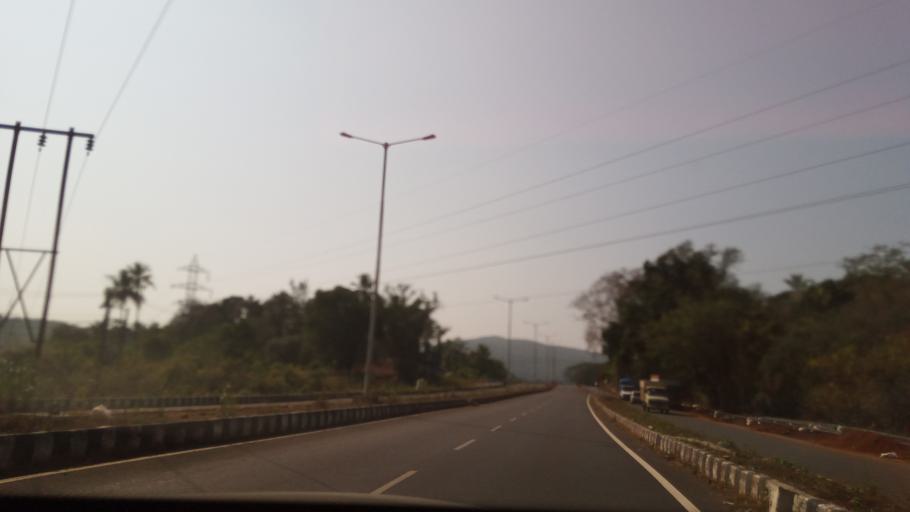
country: IN
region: Goa
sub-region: North Goa
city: Curti
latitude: 15.4201
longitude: 74.0551
